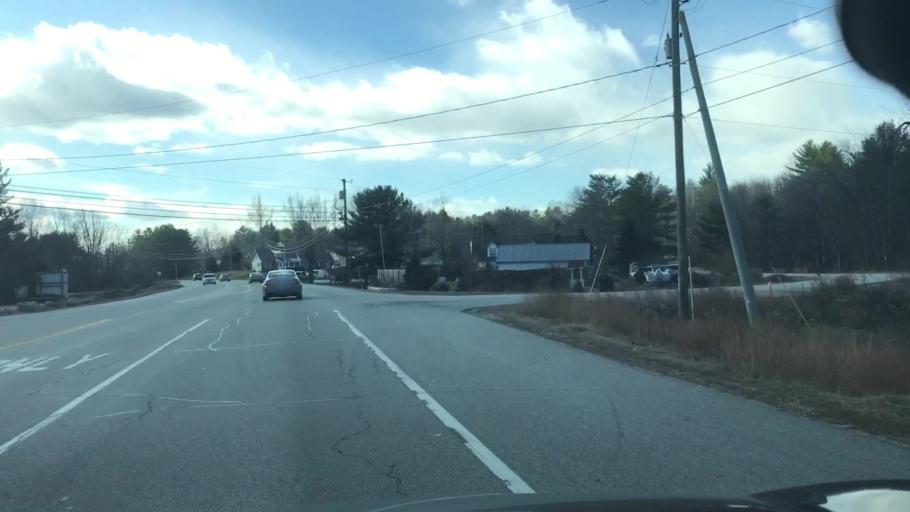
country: US
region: New Hampshire
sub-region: Merrimack County
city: Pittsfield
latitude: 43.2991
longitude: -71.3483
